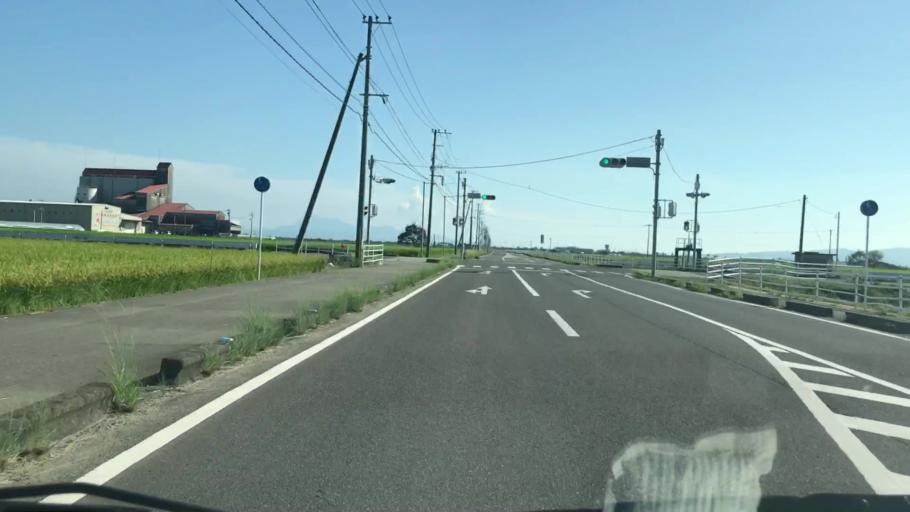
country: JP
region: Saga Prefecture
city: Okawa
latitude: 33.1755
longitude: 130.3118
